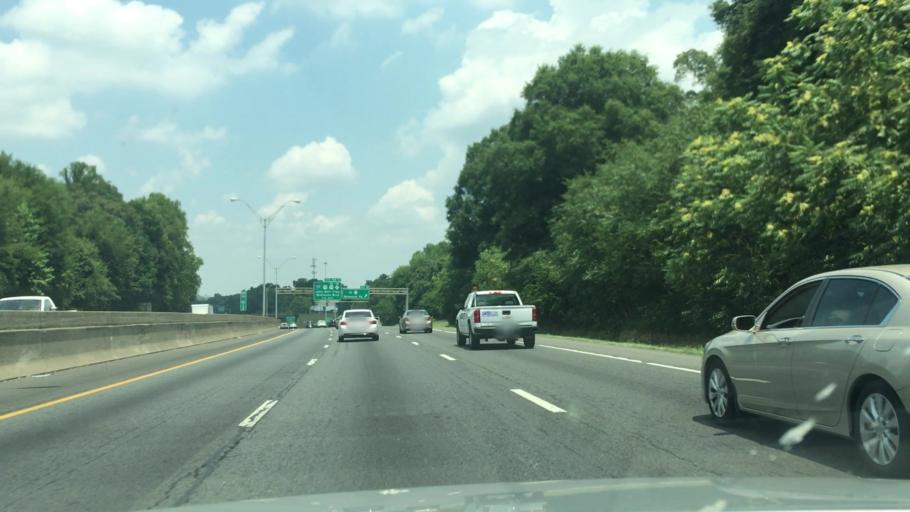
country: US
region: North Carolina
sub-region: Mecklenburg County
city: Charlotte
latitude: 35.2065
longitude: -80.8773
